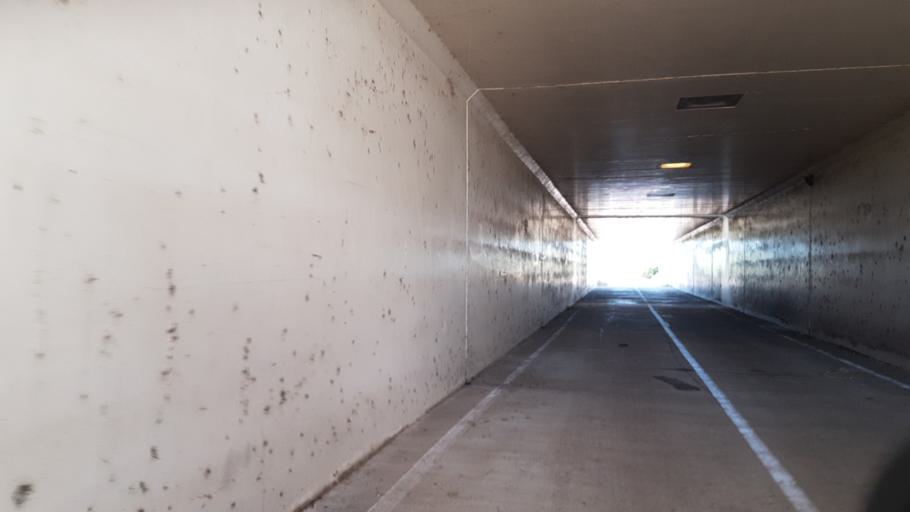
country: AU
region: Western Australia
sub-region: Kwinana
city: Wellard
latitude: -32.2937
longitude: 115.8346
